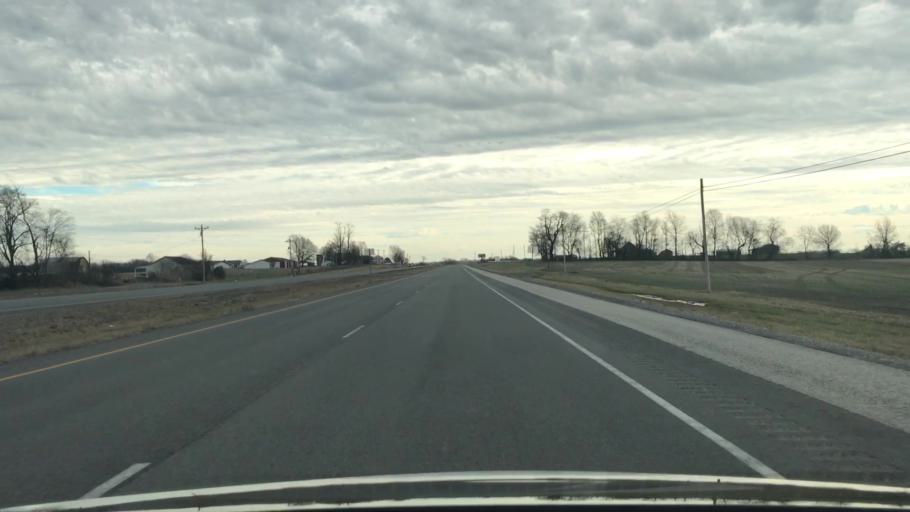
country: US
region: Kentucky
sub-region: Trigg County
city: Cadiz
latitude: 36.8864
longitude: -87.7195
